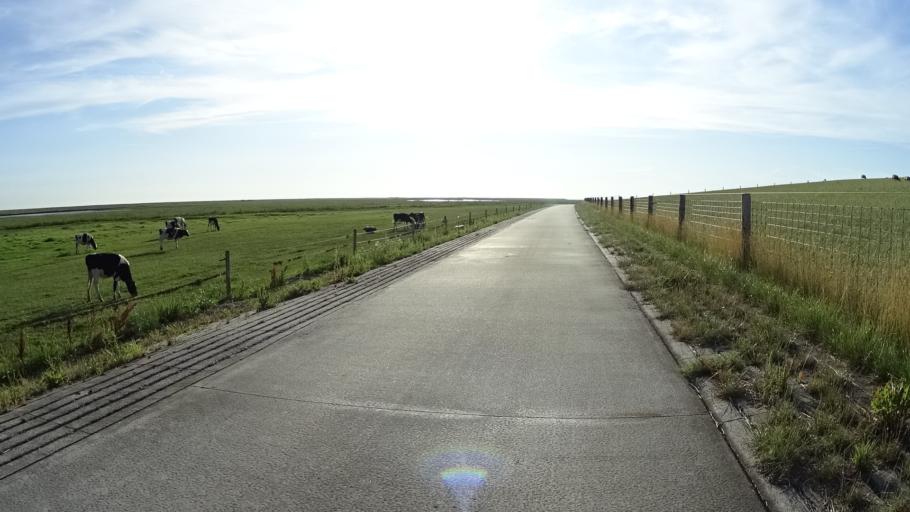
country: DE
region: Lower Saxony
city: Butjadingen
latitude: 53.6097
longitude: 8.3186
